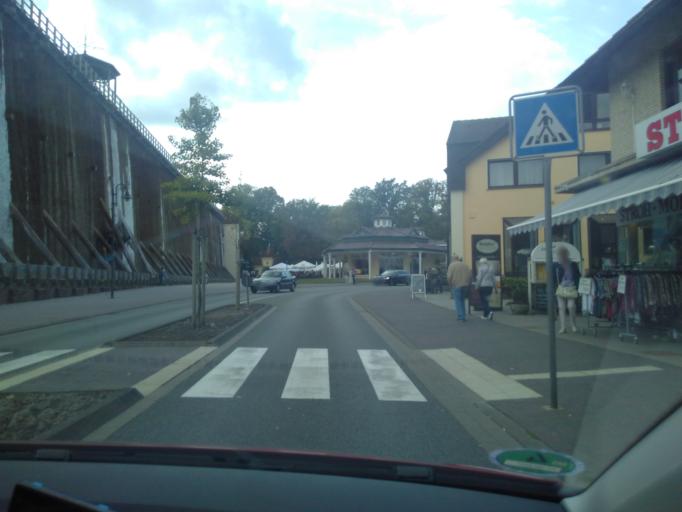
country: DE
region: Lower Saxony
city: Bad Rothenfelde
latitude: 52.1095
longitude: 8.1628
